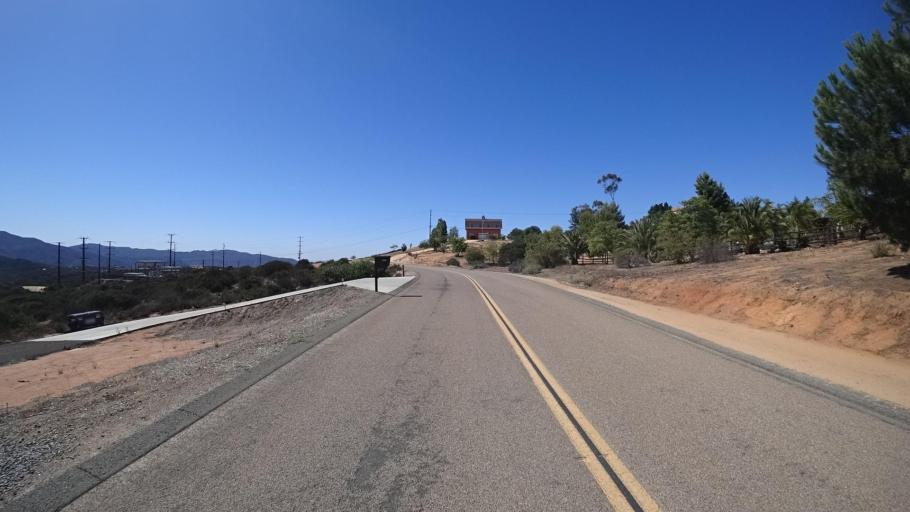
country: US
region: California
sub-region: San Diego County
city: Alpine
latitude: 32.7987
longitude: -116.7905
